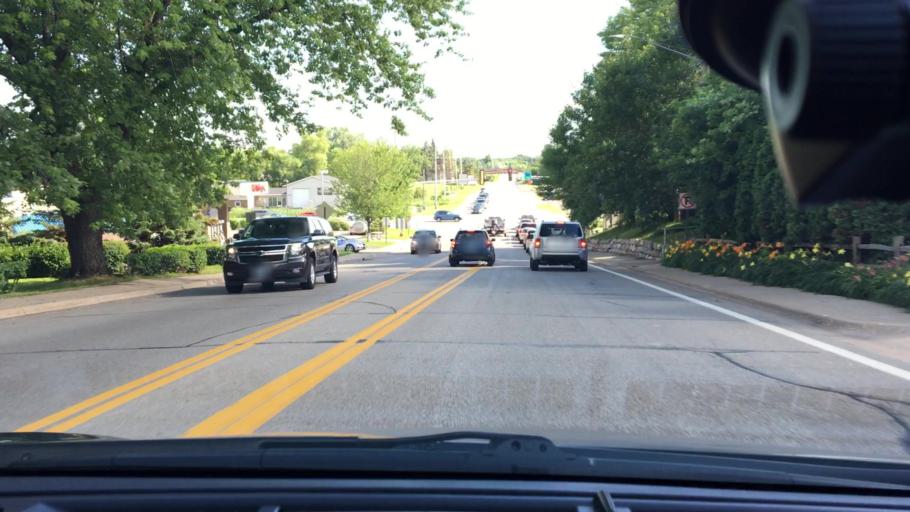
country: US
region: Minnesota
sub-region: Hennepin County
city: Saint Bonifacius
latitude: 44.9030
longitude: -93.7473
